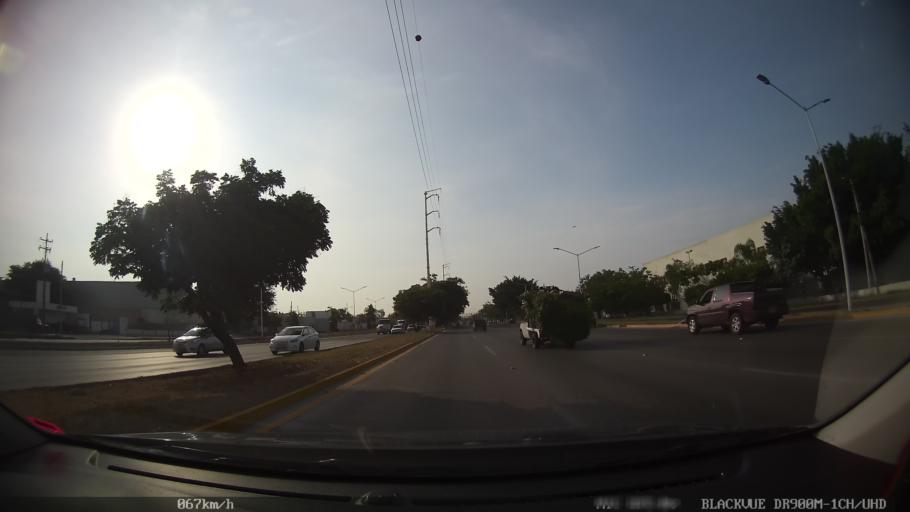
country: MX
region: Jalisco
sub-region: Zapopan
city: Zapopan
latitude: 20.7171
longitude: -103.3092
